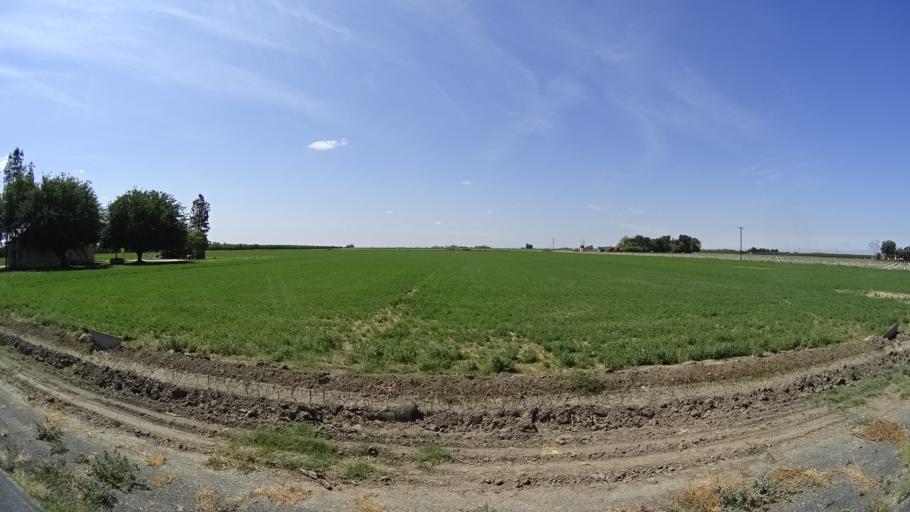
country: US
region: California
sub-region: Kings County
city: Lemoore
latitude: 36.2694
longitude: -119.7383
